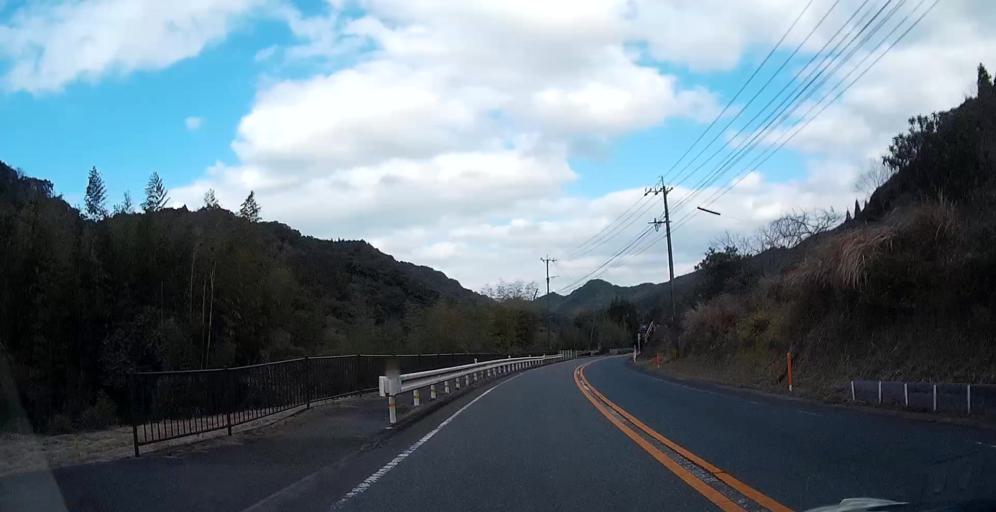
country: JP
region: Kumamoto
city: Yatsushiro
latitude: 32.3804
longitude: 130.5374
